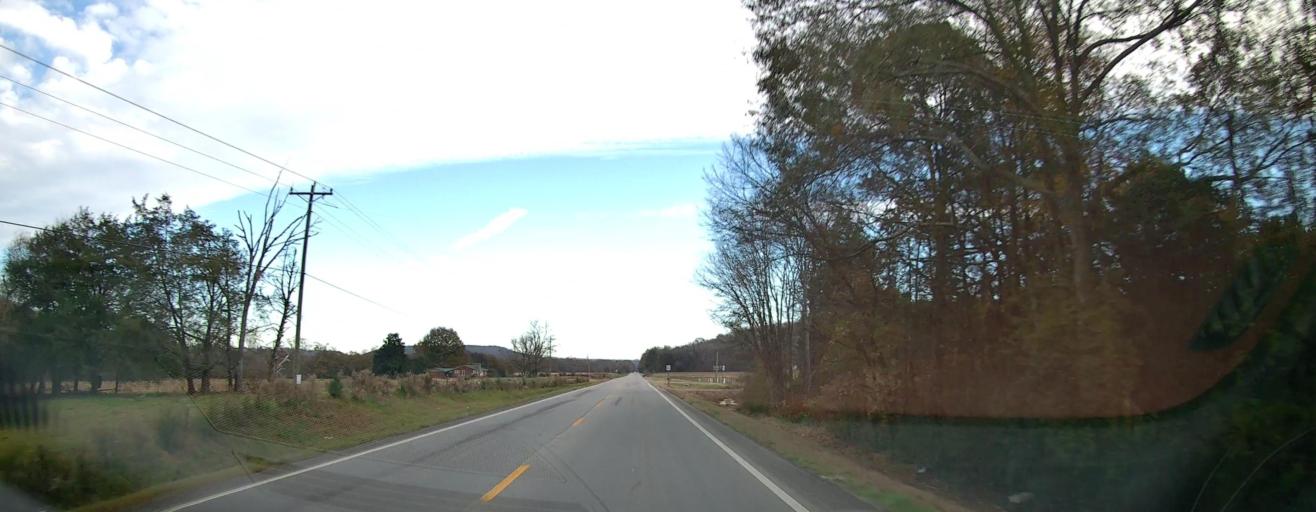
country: US
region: Alabama
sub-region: Marshall County
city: Arab
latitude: 34.4036
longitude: -86.6872
